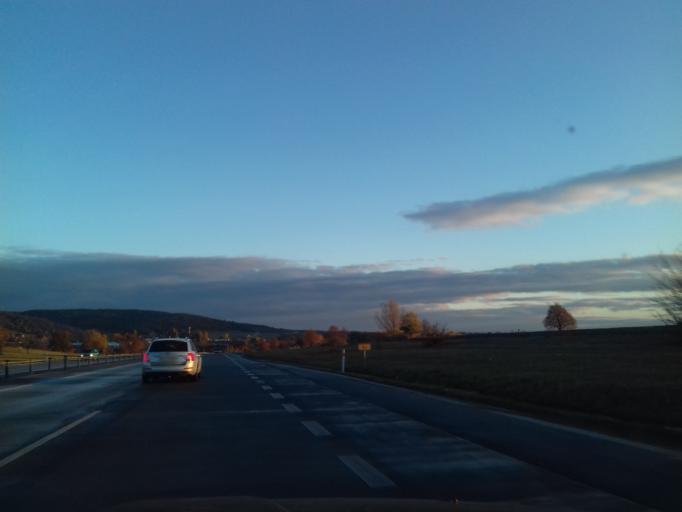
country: CZ
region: South Moravian
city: Pustimer
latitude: 49.3100
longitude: 17.0324
